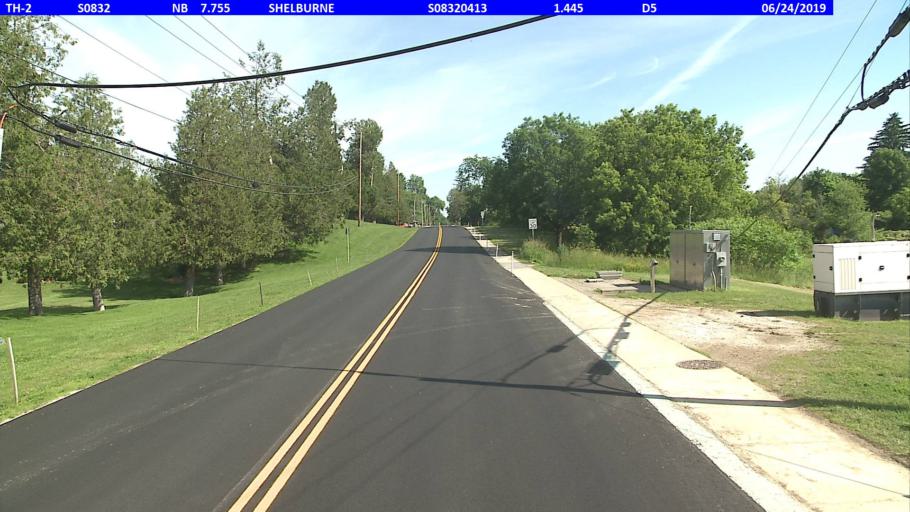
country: US
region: Vermont
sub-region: Chittenden County
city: Burlington
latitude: 44.3755
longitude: -73.2259
